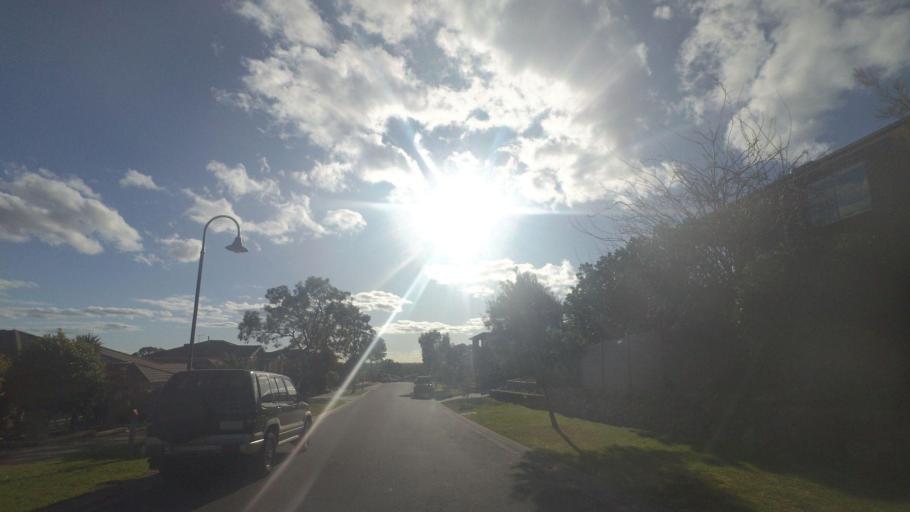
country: AU
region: Victoria
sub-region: Knox
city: Ferntree Gully
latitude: -37.9073
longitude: 145.2835
